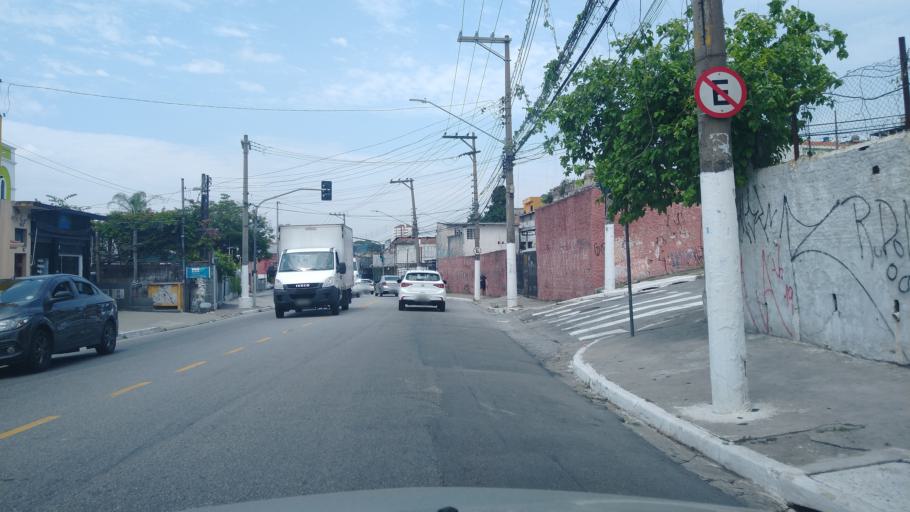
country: BR
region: Sao Paulo
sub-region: Sao Paulo
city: Sao Paulo
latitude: -23.4853
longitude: -46.6531
